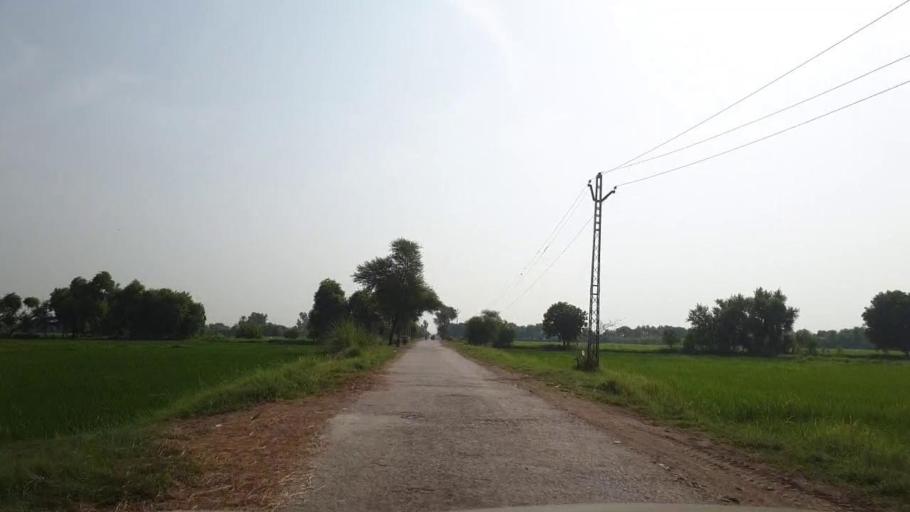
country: PK
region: Sindh
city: Larkana
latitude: 27.4538
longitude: 68.1993
